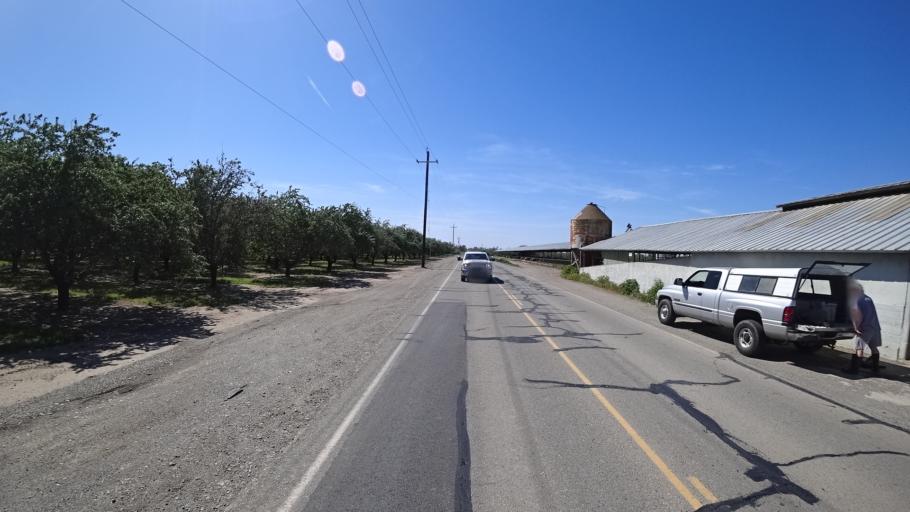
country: US
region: California
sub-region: Glenn County
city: Hamilton City
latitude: 39.7389
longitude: -122.1042
